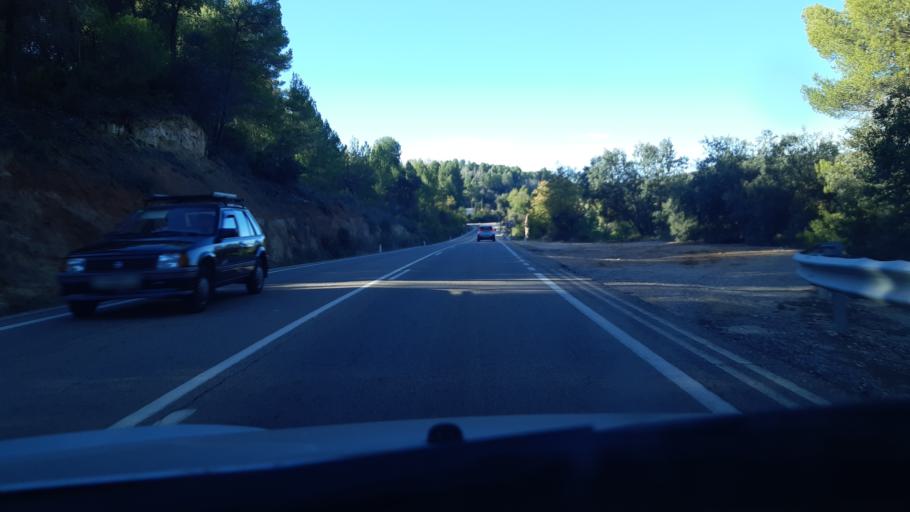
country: ES
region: Aragon
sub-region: Provincia de Teruel
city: Valderrobres
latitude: 40.8741
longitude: 0.1382
